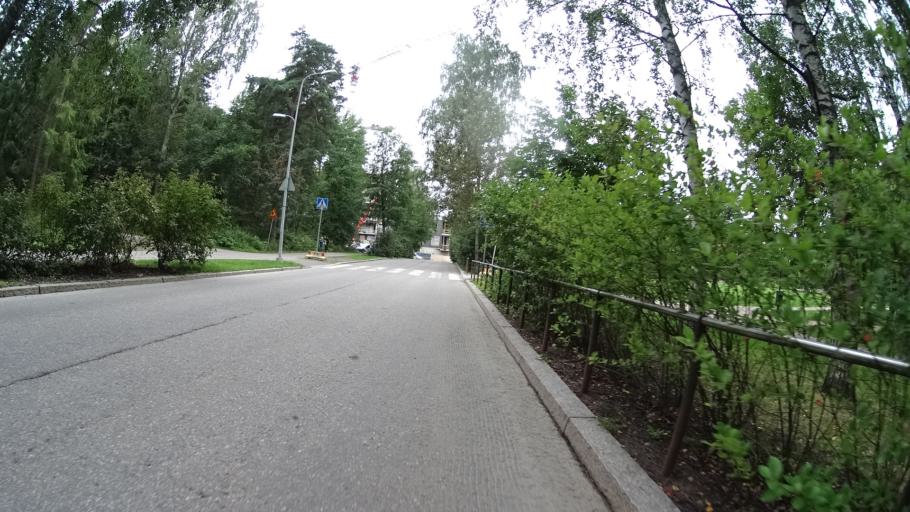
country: FI
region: Uusimaa
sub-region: Helsinki
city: Helsinki
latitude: 60.1976
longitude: 24.9047
